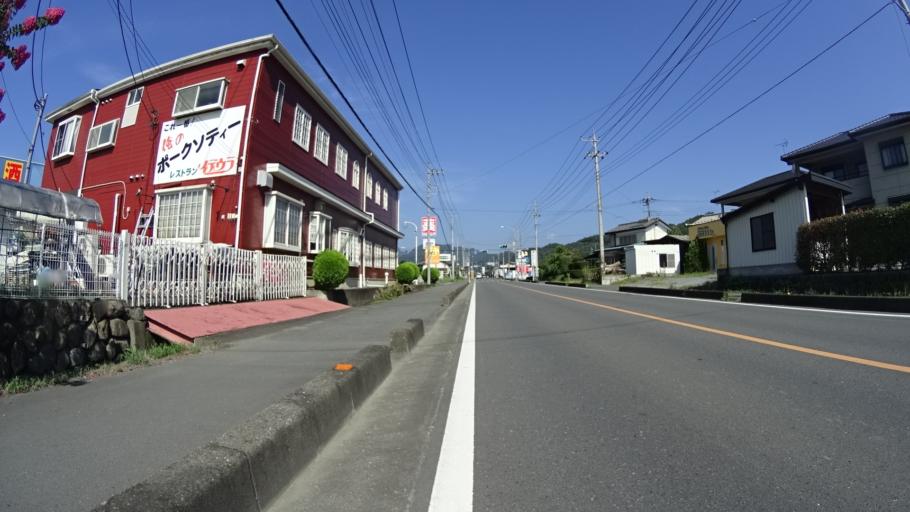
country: JP
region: Saitama
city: Chichibu
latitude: 36.0211
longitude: 139.0083
